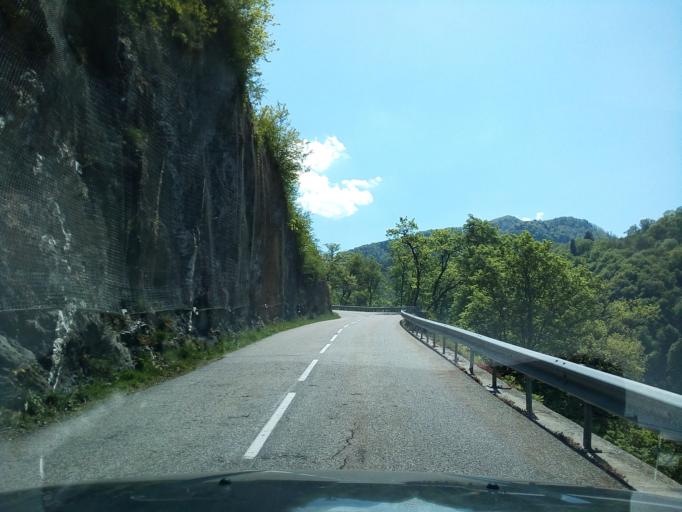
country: FR
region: Rhone-Alpes
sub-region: Departement de l'Isere
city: Domene
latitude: 45.2002
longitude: 5.8448
